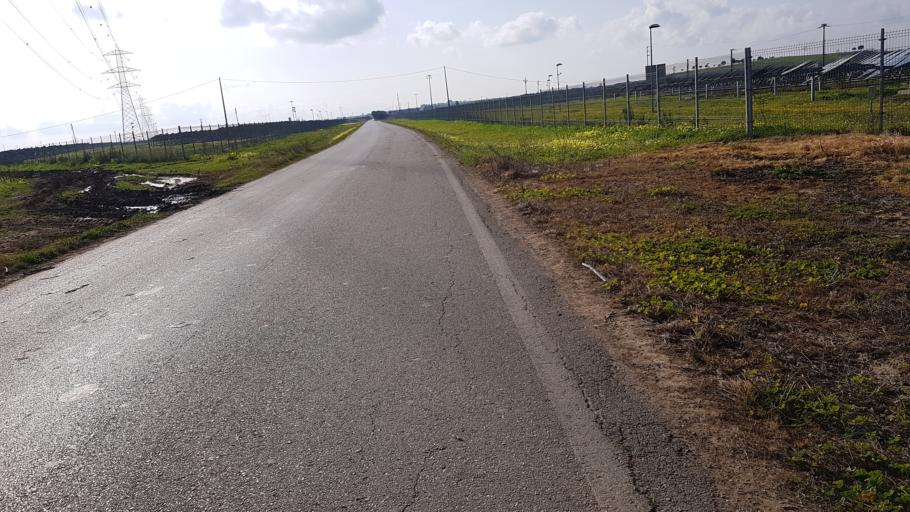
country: IT
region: Apulia
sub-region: Provincia di Brindisi
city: La Rosa
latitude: 40.5911
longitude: 17.9032
